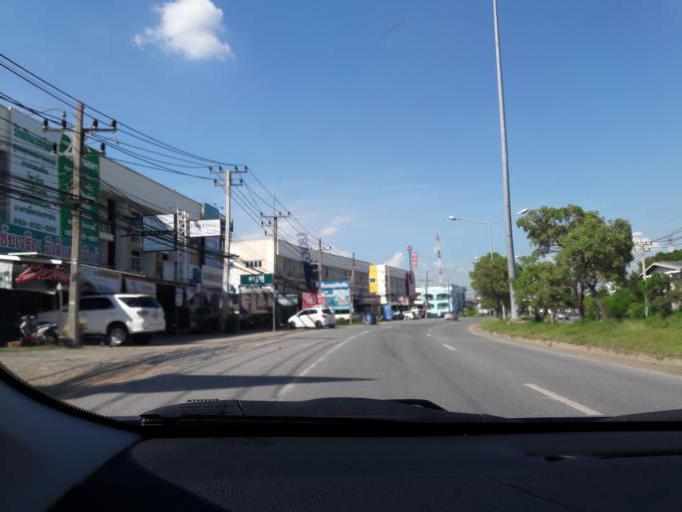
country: TH
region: Ang Thong
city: Ang Thong
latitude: 14.5820
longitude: 100.4528
